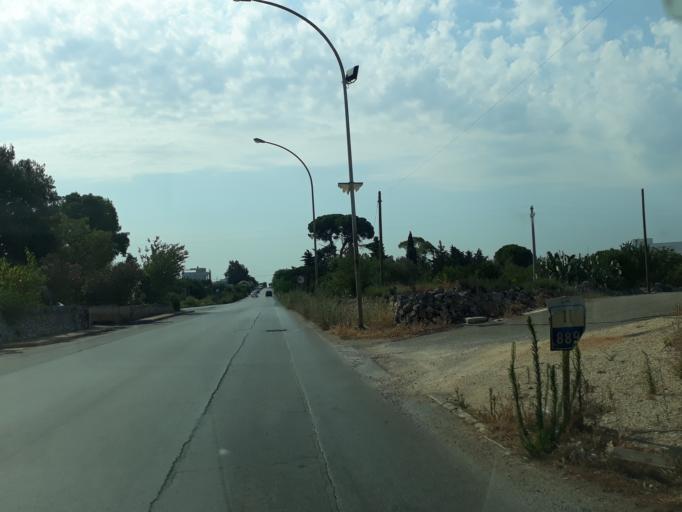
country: IT
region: Apulia
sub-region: Provincia di Brindisi
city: Carovigno
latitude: 40.6987
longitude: 17.6656
